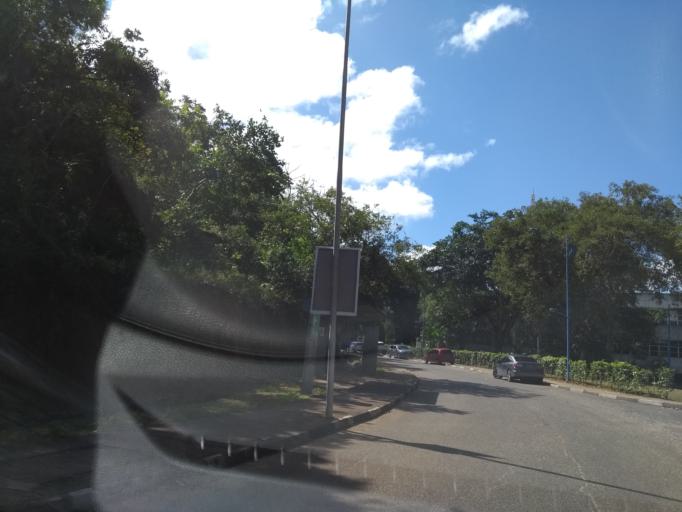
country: BR
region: Bahia
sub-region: Salvador
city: Salvador
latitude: -13.0005
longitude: -38.5088
